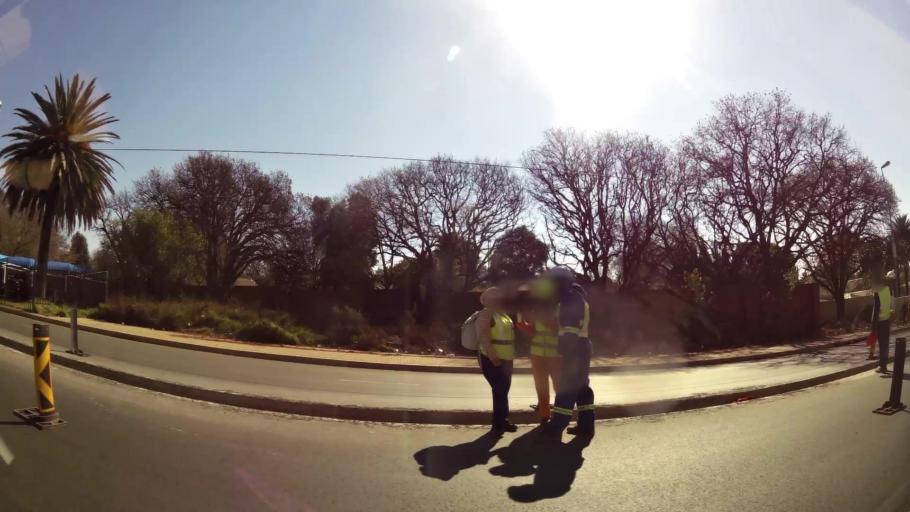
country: ZA
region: Gauteng
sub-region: City of Johannesburg Metropolitan Municipality
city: Johannesburg
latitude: -26.1738
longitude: 28.0681
